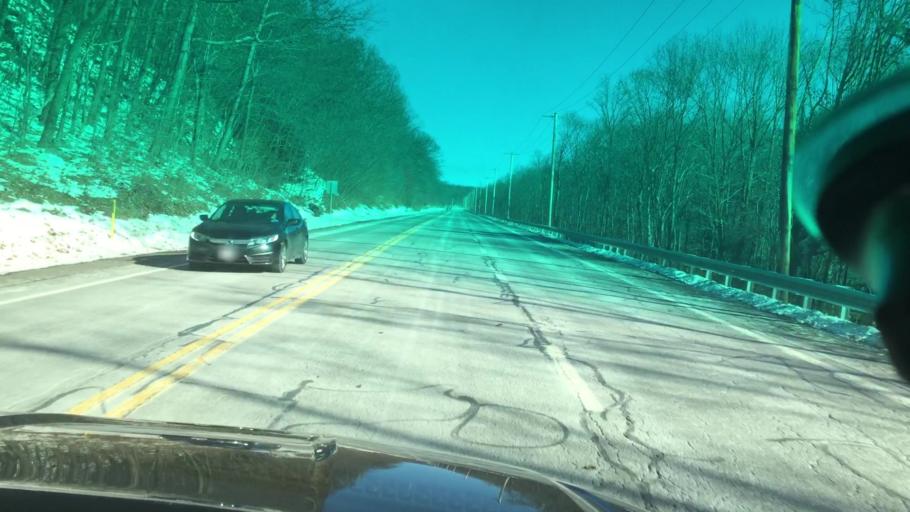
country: US
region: Pennsylvania
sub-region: Luzerne County
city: Oakdale
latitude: 41.0183
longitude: -75.9446
